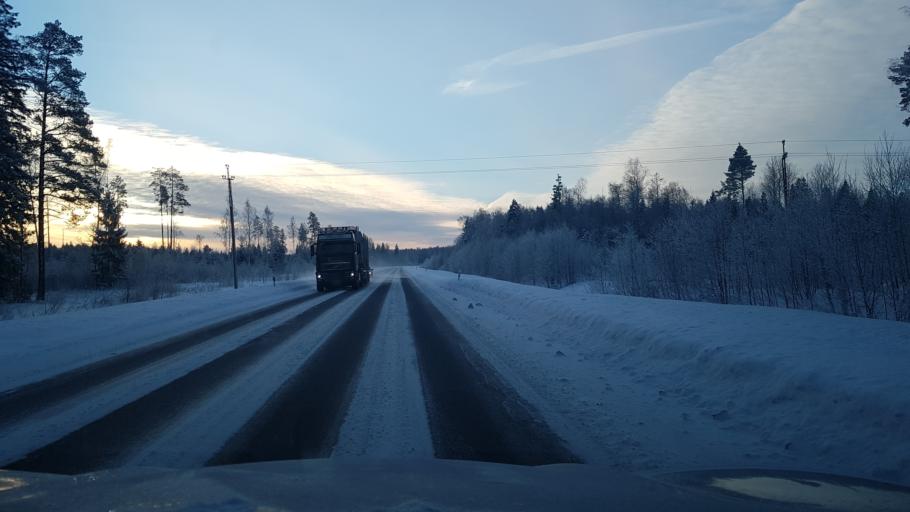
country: EE
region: Ida-Virumaa
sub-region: Johvi vald
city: Johvi
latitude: 59.3577
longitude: 27.4639
